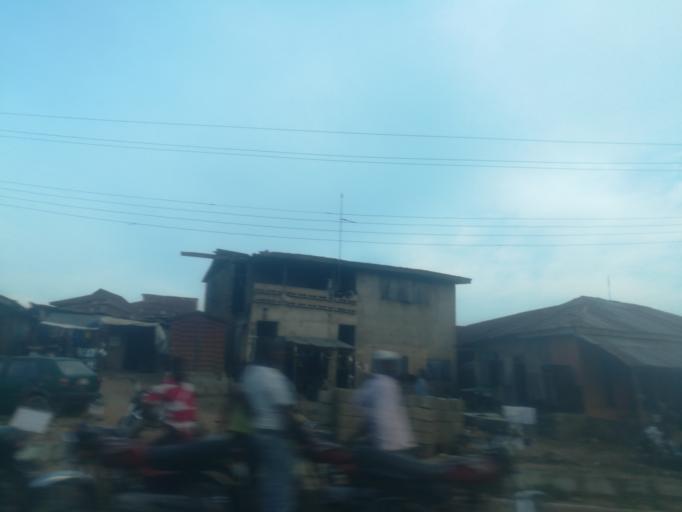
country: NG
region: Ogun
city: Abeokuta
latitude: 7.1607
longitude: 3.3308
